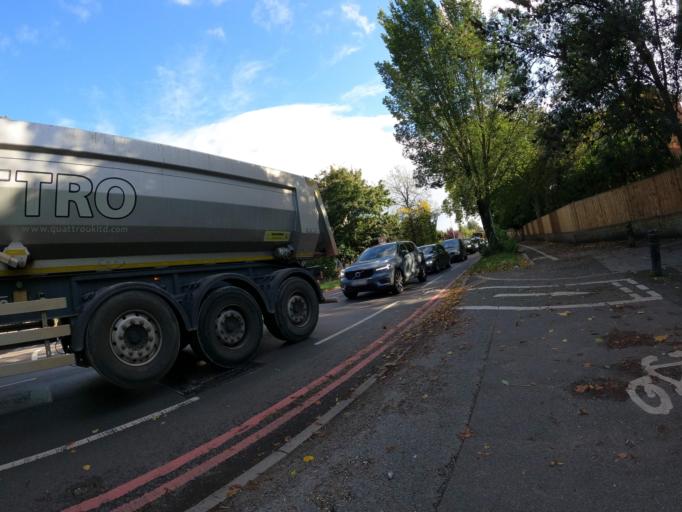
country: GB
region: England
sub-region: Greater London
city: Ealing
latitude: 51.5078
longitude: -0.2916
